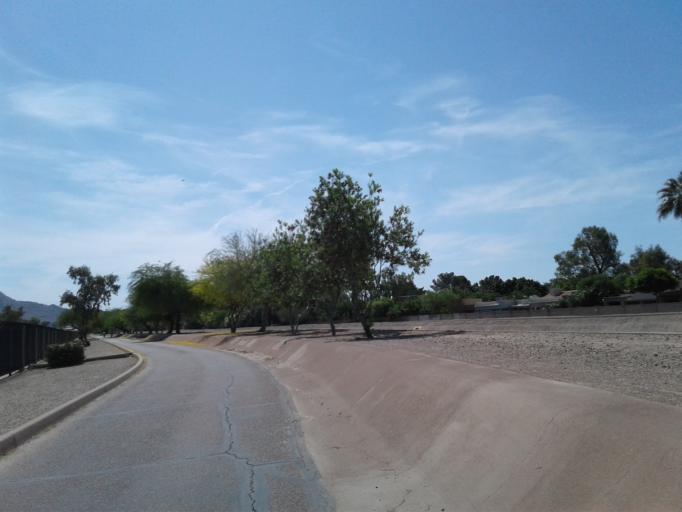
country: US
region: Arizona
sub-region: Maricopa County
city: Phoenix
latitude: 33.5606
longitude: -112.0727
